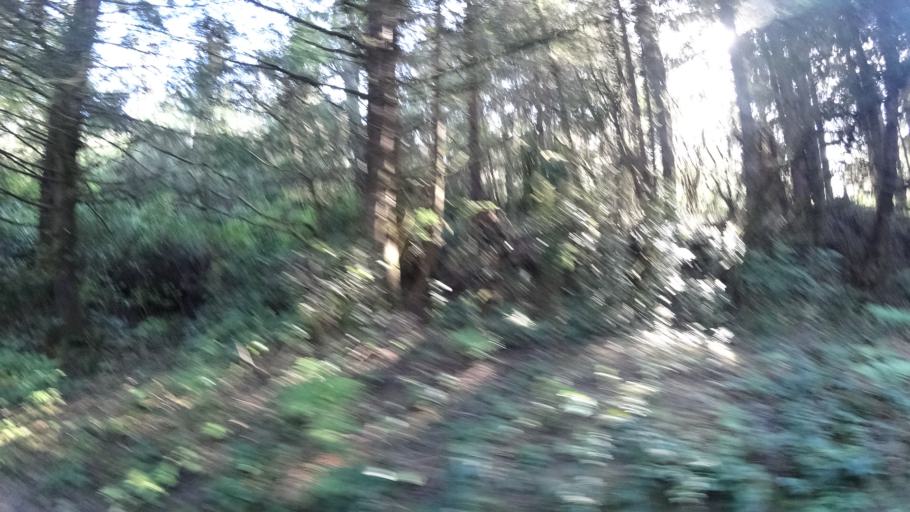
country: US
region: Oregon
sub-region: Douglas County
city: Reedsport
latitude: 43.7484
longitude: -124.1758
